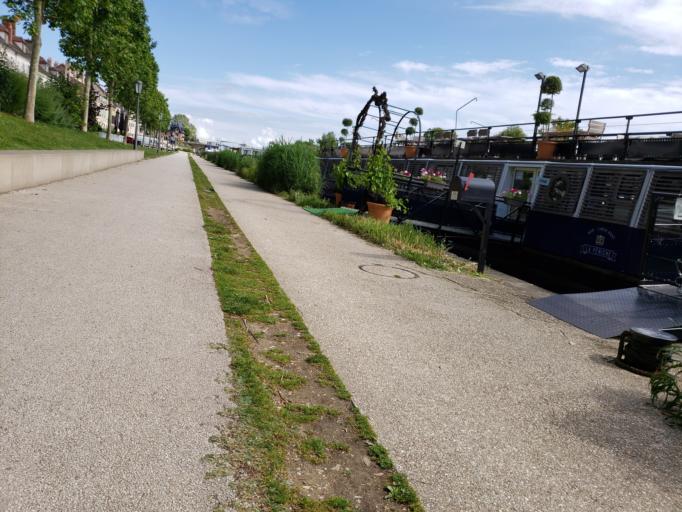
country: FR
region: Bourgogne
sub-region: Departement de l'Yonne
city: Auxerre
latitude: 47.7985
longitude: 3.5746
